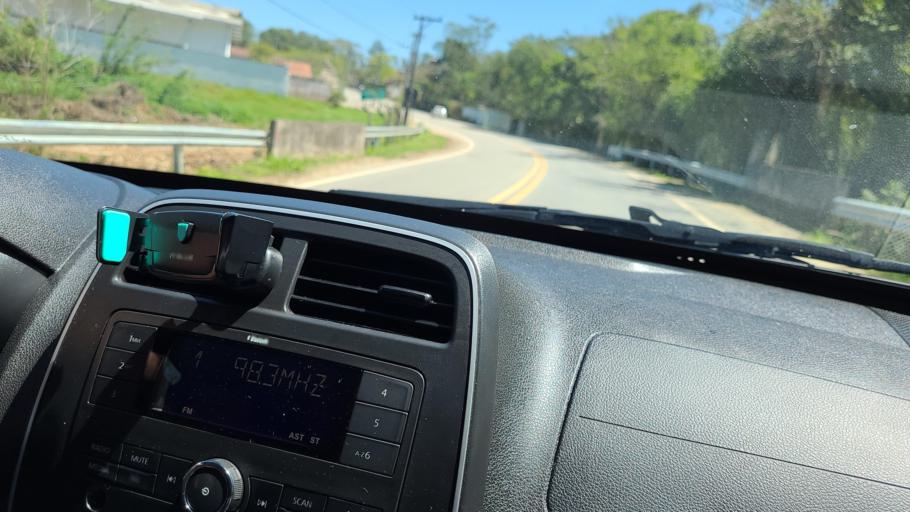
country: BR
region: Sao Paulo
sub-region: Tremembe
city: Tremembe
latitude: -22.8869
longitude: -45.5451
